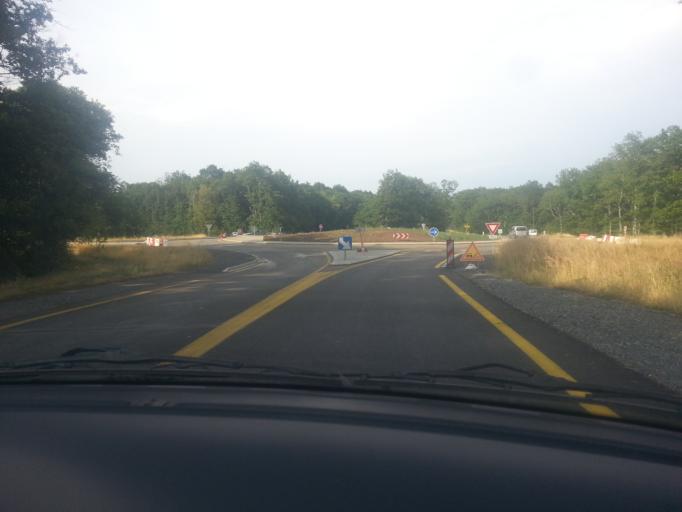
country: FR
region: Auvergne
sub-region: Departement de l'Allier
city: Brugheas
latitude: 46.0954
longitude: 3.3476
